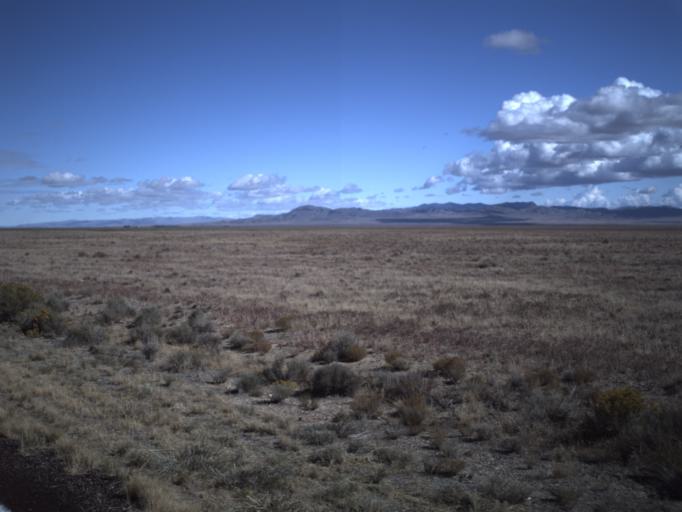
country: US
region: Nevada
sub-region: White Pine County
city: McGill
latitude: 38.9683
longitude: -114.0338
